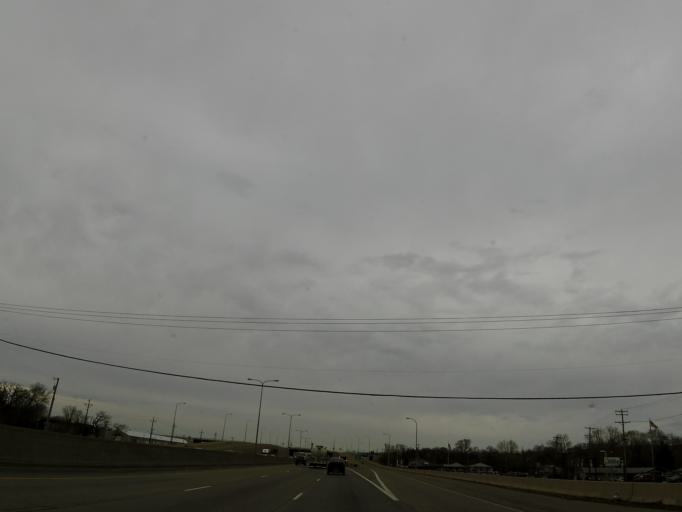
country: US
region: Minnesota
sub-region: Washington County
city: Newport
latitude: 44.8667
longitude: -92.9987
